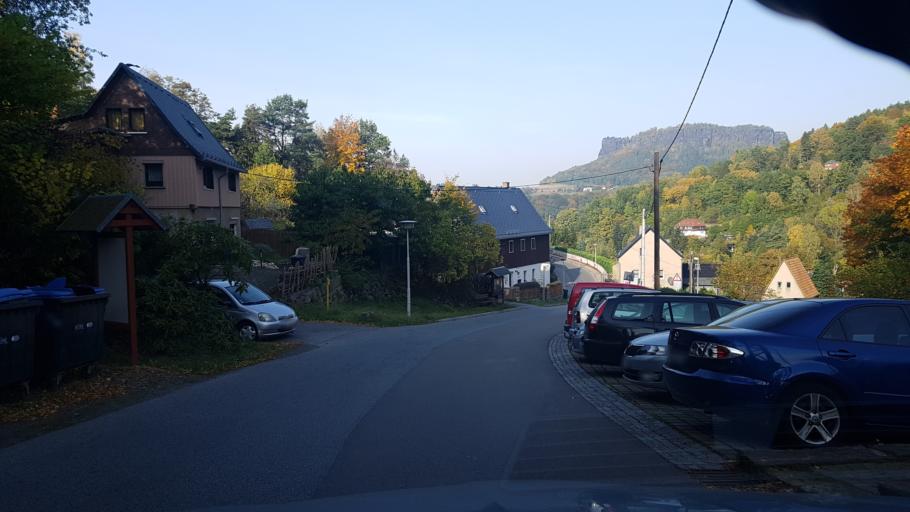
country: DE
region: Saxony
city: Konigstein
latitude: 50.9125
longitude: 14.0743
